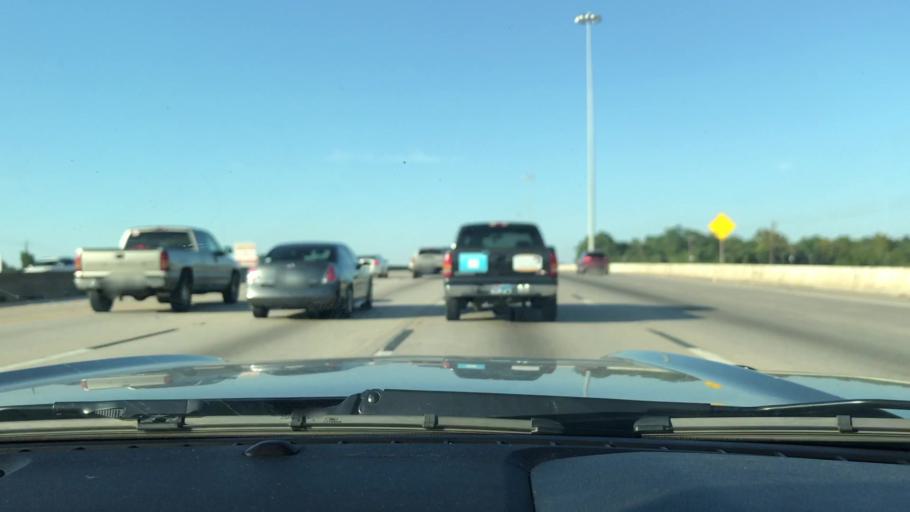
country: US
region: Texas
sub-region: Harris County
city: Aldine
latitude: 29.8886
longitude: -95.3191
